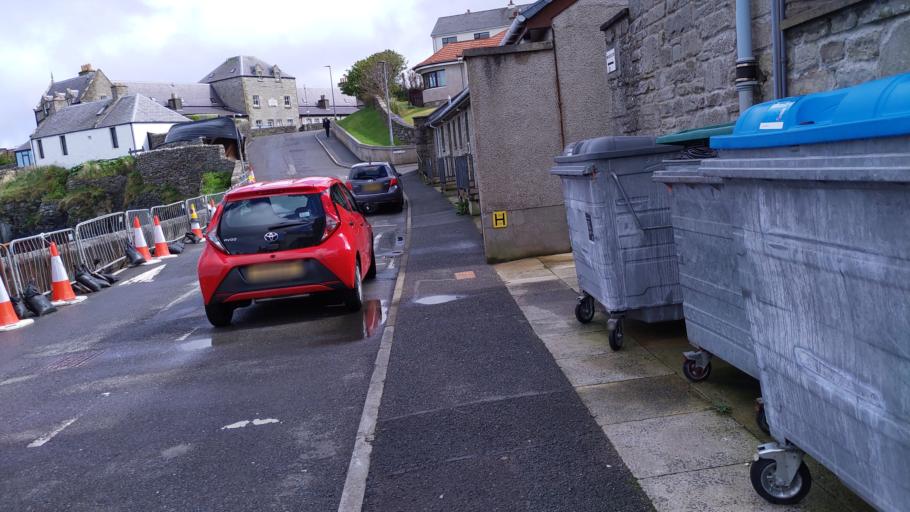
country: GB
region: Scotland
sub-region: Shetland Islands
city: Shetland
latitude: 60.1523
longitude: -1.1369
